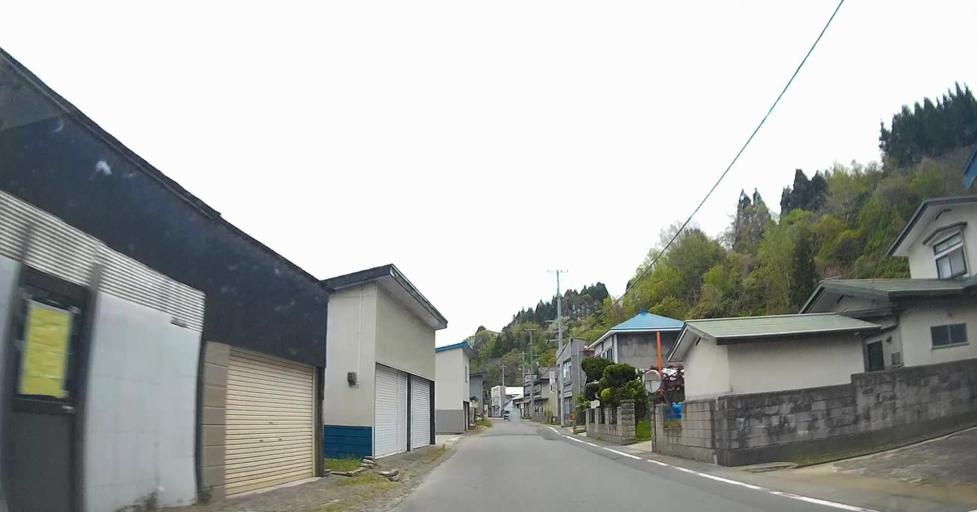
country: JP
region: Aomori
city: Shimokizukuri
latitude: 41.2045
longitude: 140.4269
